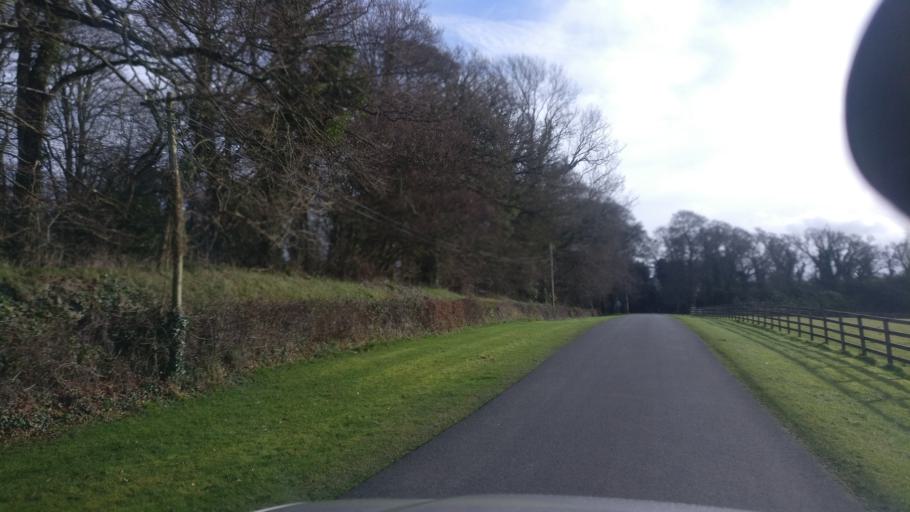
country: IE
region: Leinster
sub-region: Kilkenny
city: Thomastown
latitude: 52.5299
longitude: -7.1712
